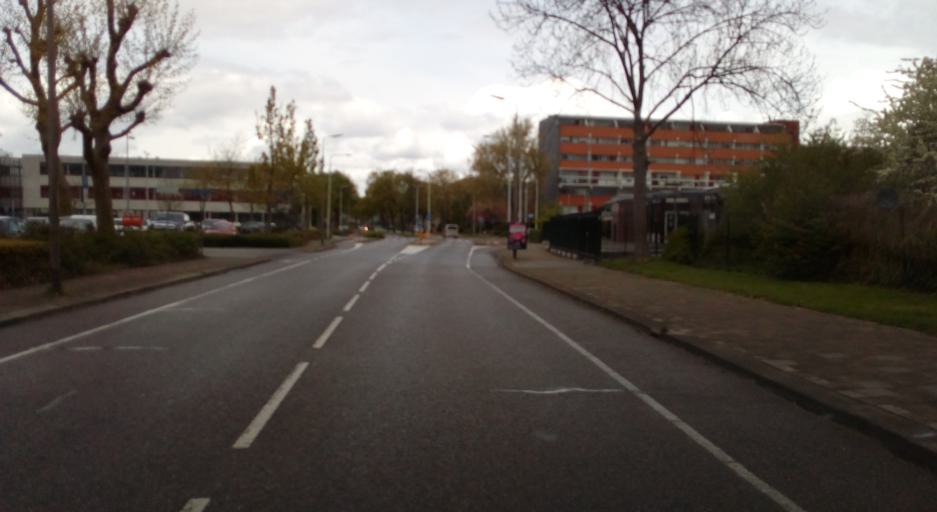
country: NL
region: South Holland
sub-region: Gemeente Dordrecht
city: Dordrecht
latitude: 51.8218
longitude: 4.6573
